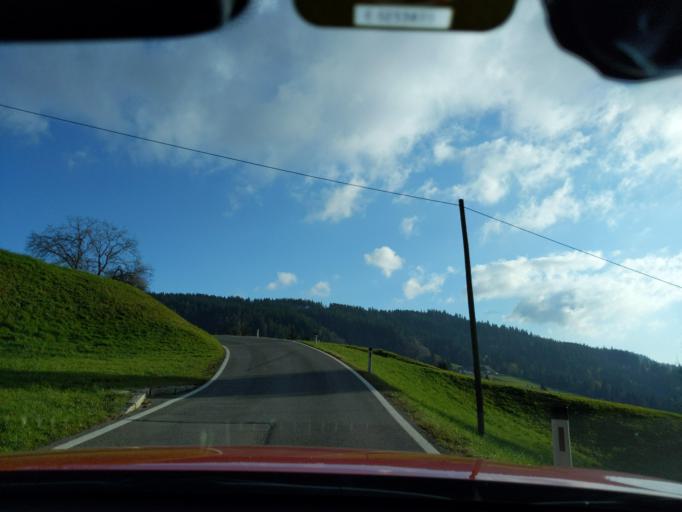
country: AT
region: Vorarlberg
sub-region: Politischer Bezirk Bregenz
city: Eichenberg
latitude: 47.5467
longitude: 9.7881
